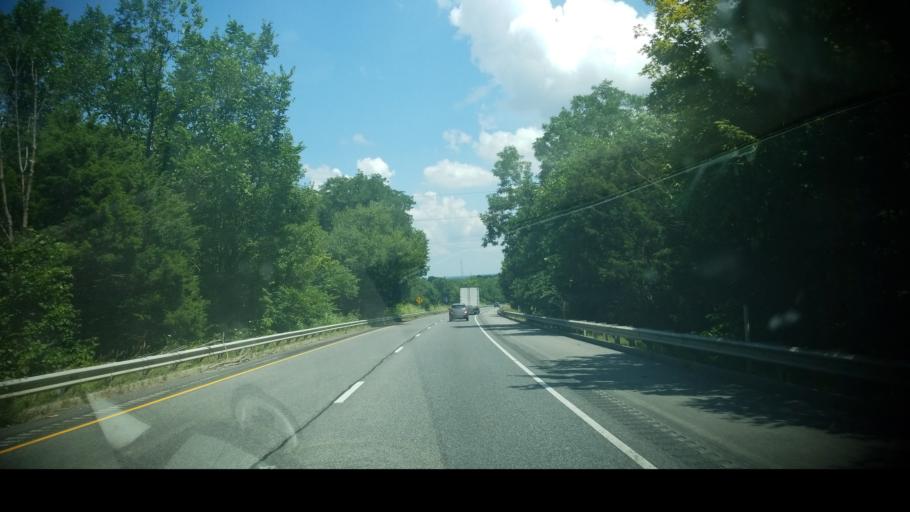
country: US
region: Indiana
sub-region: Floyd County
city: New Albany
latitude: 38.3010
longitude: -85.8517
